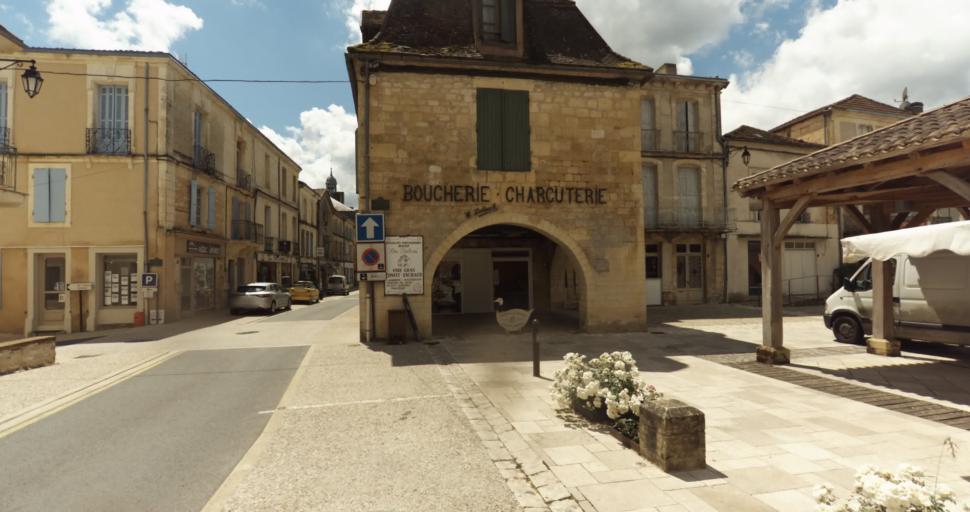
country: FR
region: Aquitaine
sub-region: Departement de la Dordogne
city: Beaumont-du-Perigord
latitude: 44.7688
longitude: 0.7676
